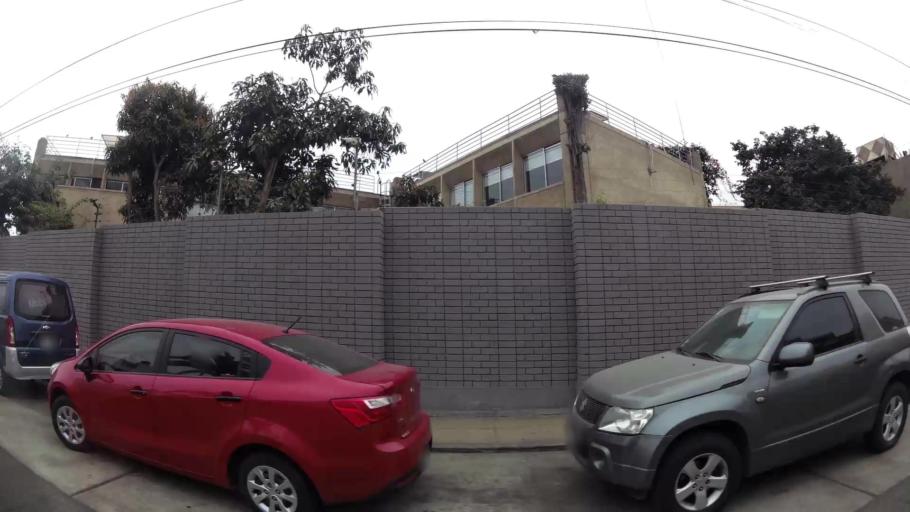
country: PE
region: Lima
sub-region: Lima
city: Surco
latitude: -12.1295
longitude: -76.9983
